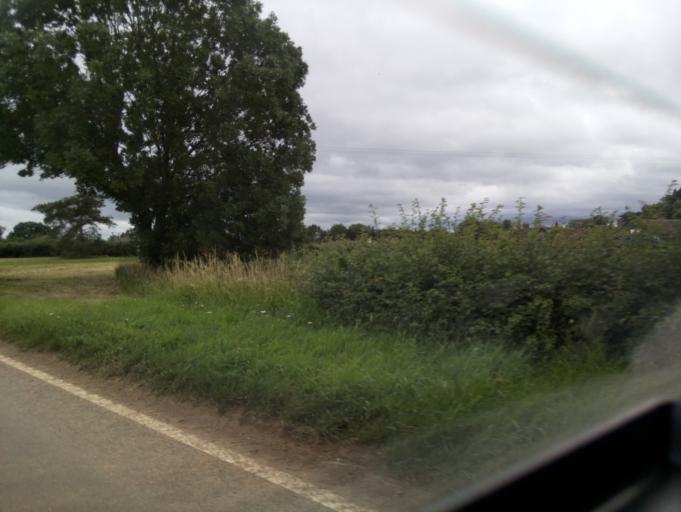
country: GB
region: England
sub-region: Worcestershire
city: Kempsey
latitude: 52.1163
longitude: -2.2220
